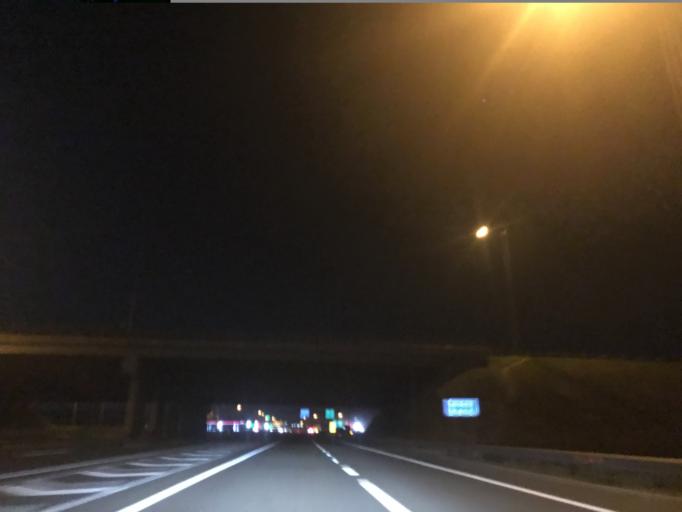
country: TR
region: Nigde
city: Ulukisla
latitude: 37.6448
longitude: 34.3566
